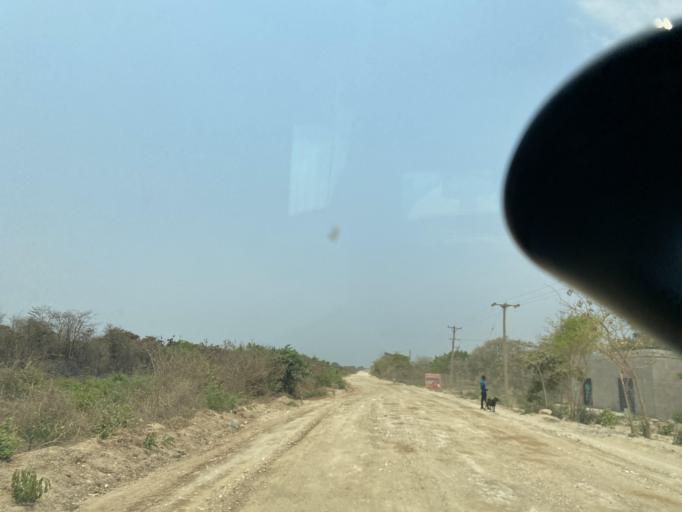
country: ZM
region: Lusaka
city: Lusaka
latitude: -15.5242
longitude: 28.3420
